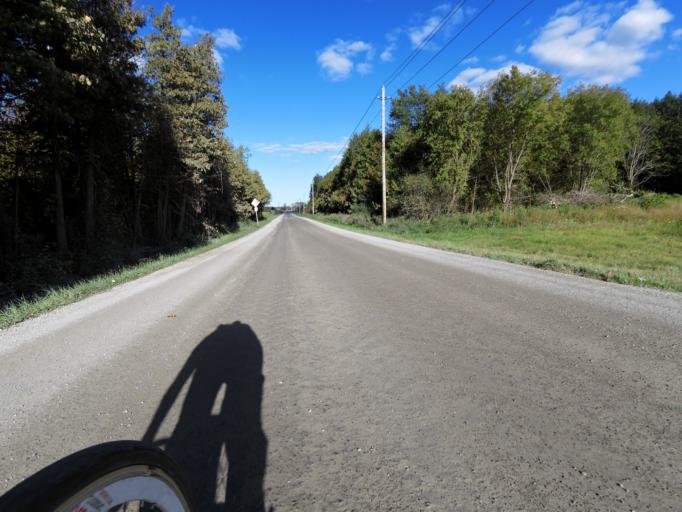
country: CA
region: Ontario
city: Bells Corners
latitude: 45.1127
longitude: -75.7114
